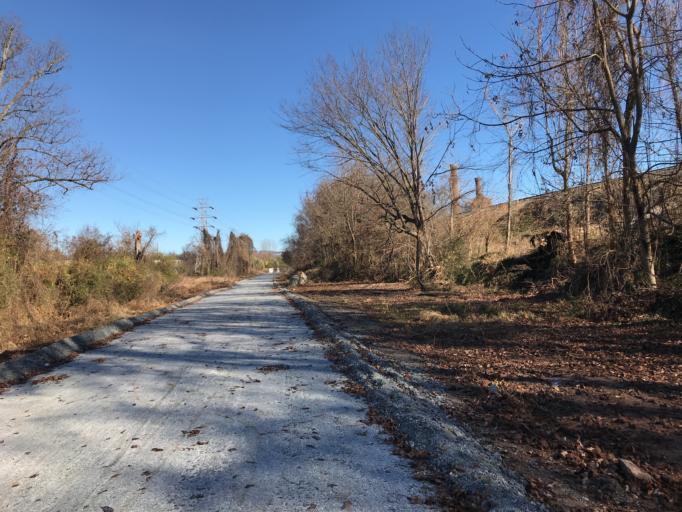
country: US
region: South Carolina
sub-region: Greenville County
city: Sans Souci
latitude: 34.8687
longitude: -82.4151
